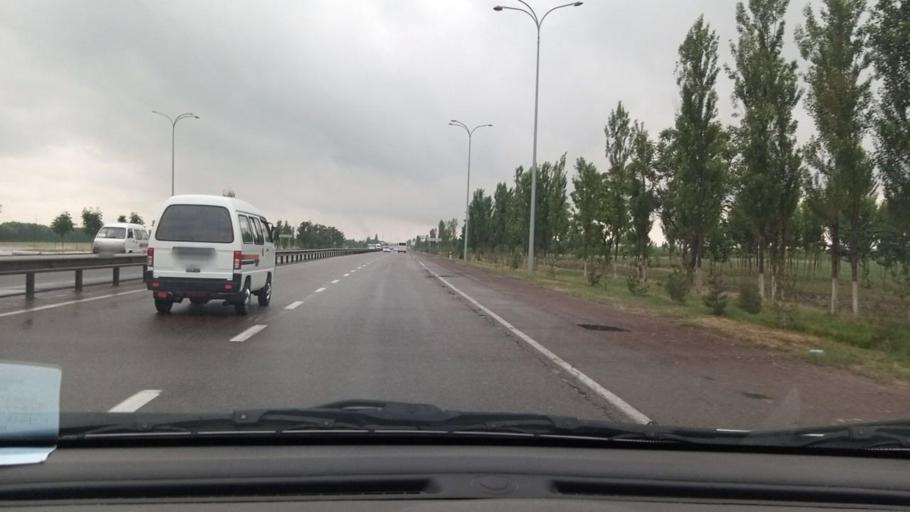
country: UZ
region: Toshkent
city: Ohangaron
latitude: 40.9148
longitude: 69.6085
